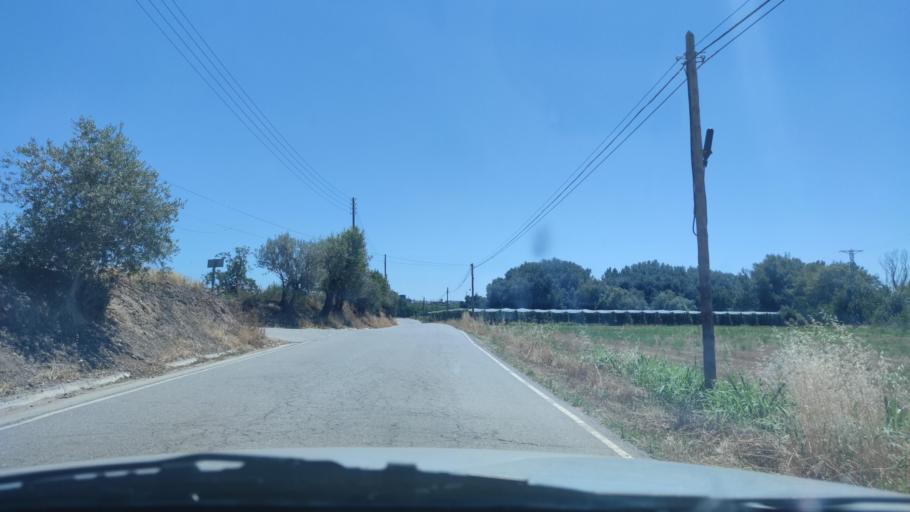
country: ES
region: Catalonia
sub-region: Provincia de Lleida
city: Lleida
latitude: 41.6292
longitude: 0.6556
